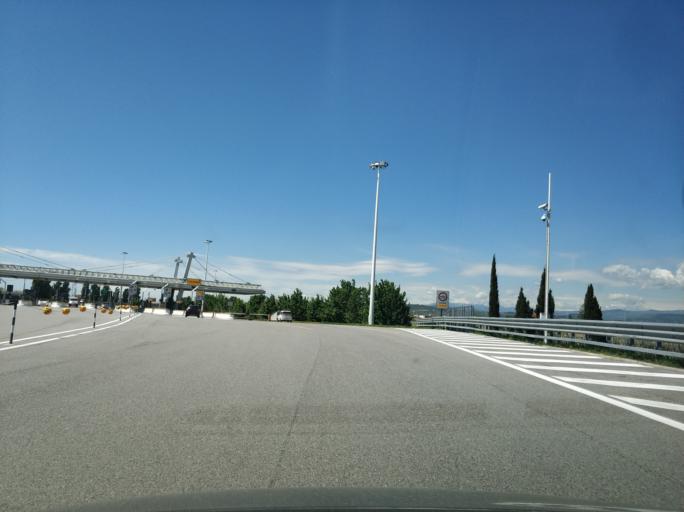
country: IT
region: Veneto
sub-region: Provincia di Verona
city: Soave
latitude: 45.4070
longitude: 11.2535
